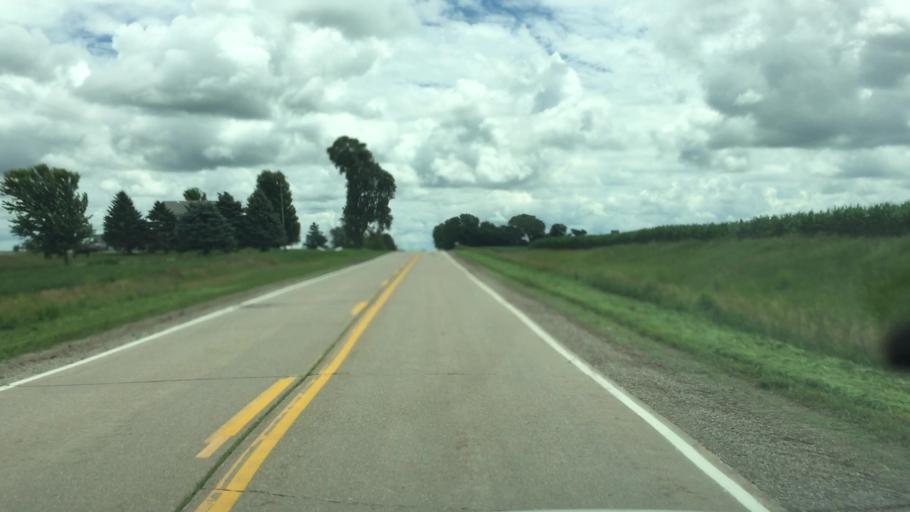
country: US
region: Iowa
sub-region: Jasper County
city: Monroe
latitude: 41.5806
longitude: -93.1483
